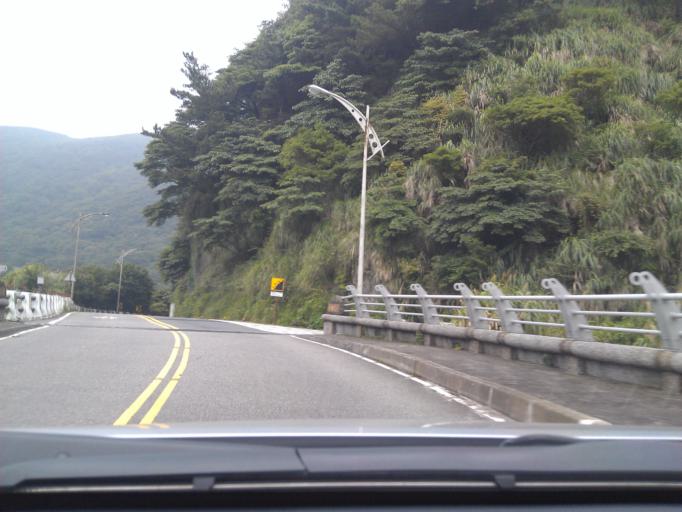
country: TW
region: Taipei
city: Taipei
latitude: 25.1763
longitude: 121.5444
